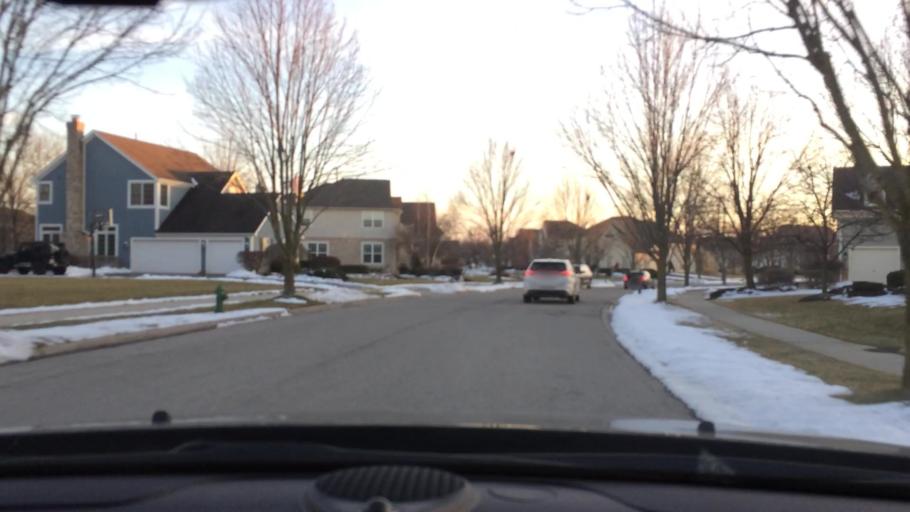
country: US
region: Ohio
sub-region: Franklin County
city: Hilliard
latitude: 40.0832
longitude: -83.1654
